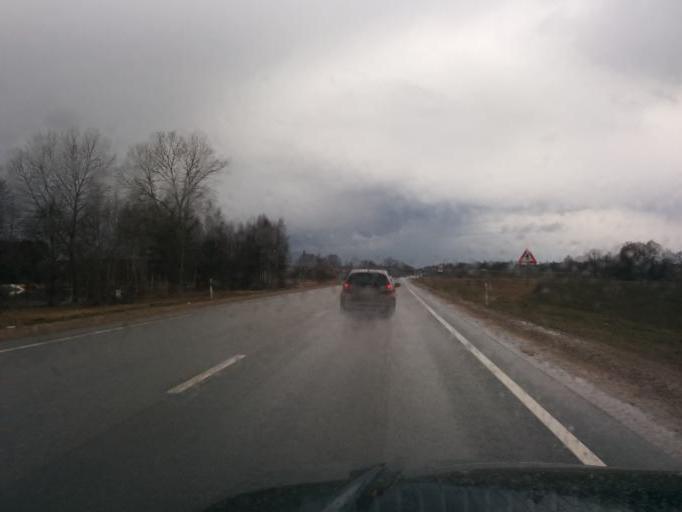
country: LV
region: Babite
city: Pinki
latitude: 56.8740
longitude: 23.9589
